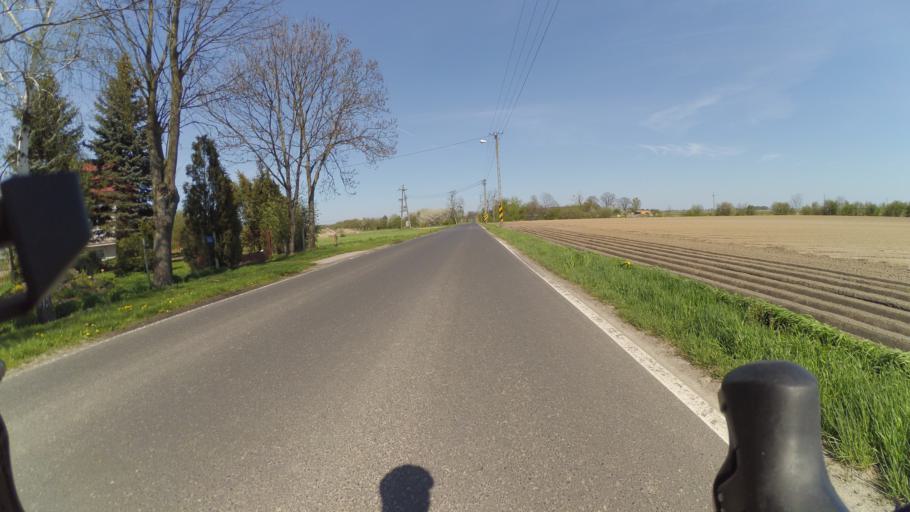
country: PL
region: Masovian Voivodeship
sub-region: Powiat warszawski zachodni
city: Leszno
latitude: 52.2478
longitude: 20.5543
